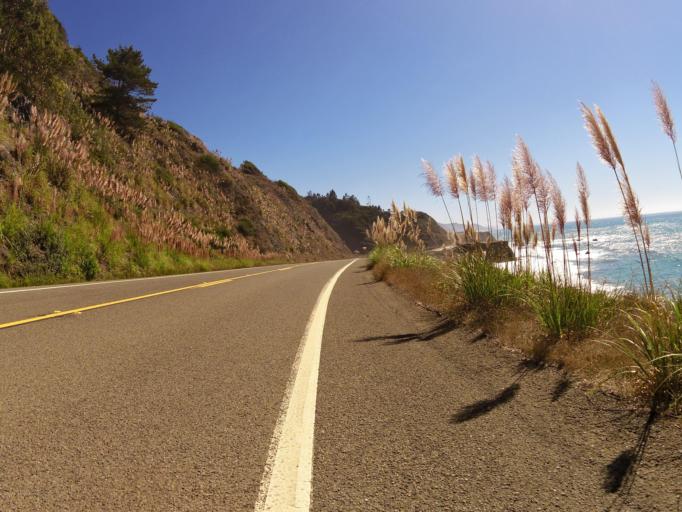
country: US
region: California
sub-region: Mendocino County
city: Fort Bragg
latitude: 39.7061
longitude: -123.8047
